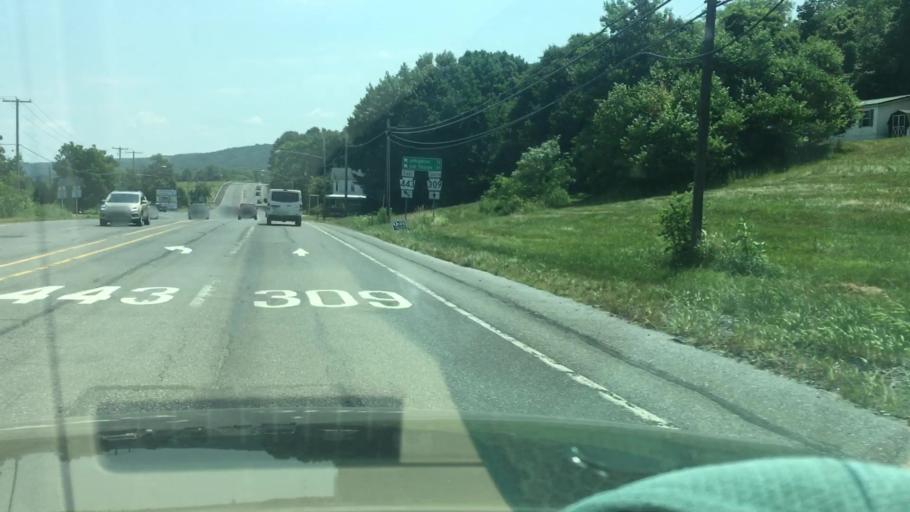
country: US
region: Pennsylvania
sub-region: Schuylkill County
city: Tamaqua
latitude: 40.7555
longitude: -75.9292
